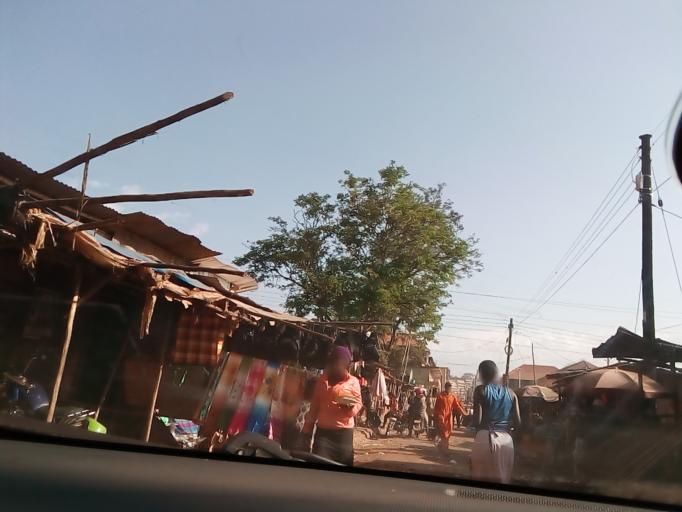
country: UG
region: Central Region
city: Masaka
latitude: -0.3483
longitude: 31.7398
